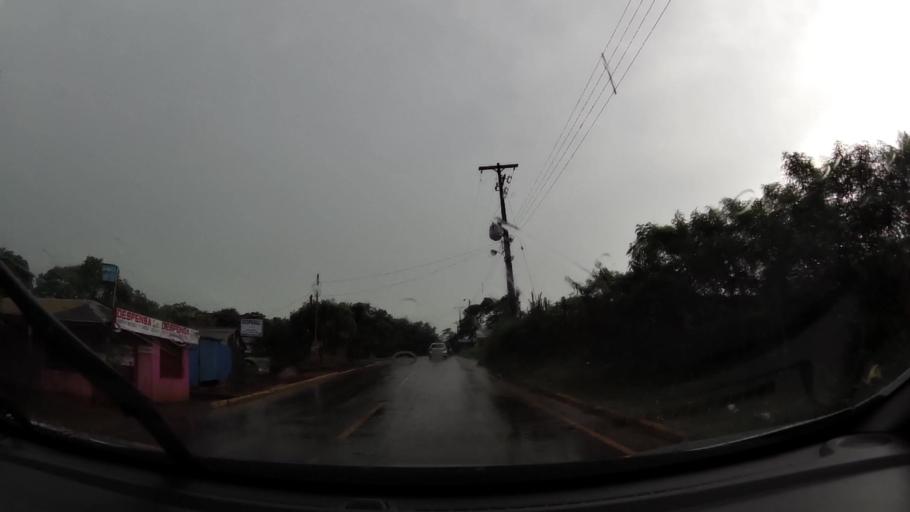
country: PY
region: Alto Parana
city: Presidente Franco
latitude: -25.5385
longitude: -54.6781
